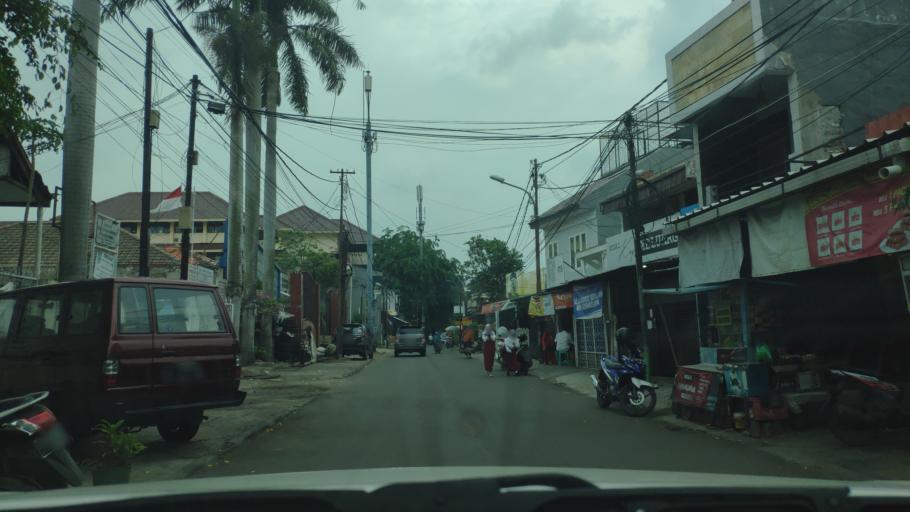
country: ID
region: Jakarta Raya
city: Jakarta
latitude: -6.1919
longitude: 106.7945
